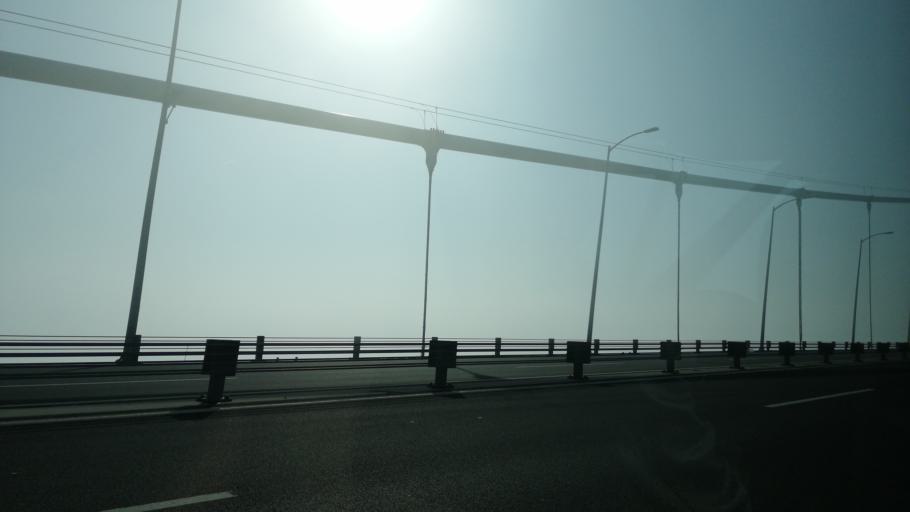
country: TR
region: Yalova
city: Altinova
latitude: 40.7537
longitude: 29.5155
